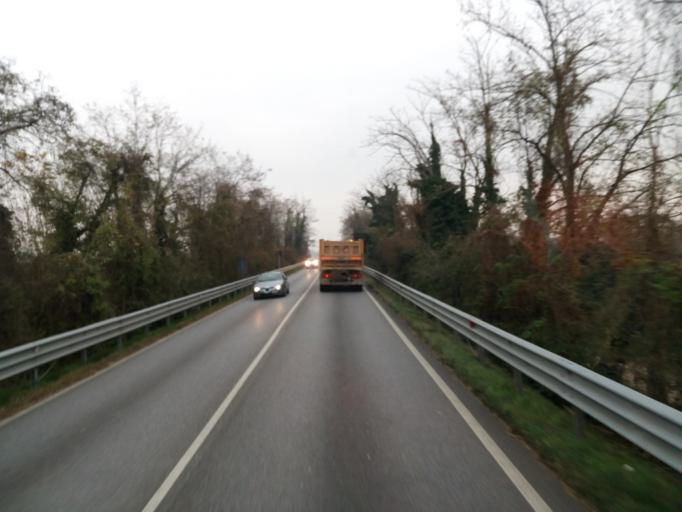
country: IT
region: Friuli Venezia Giulia
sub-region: Provincia di Udine
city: Pradamano
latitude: 46.0172
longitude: 13.3078
